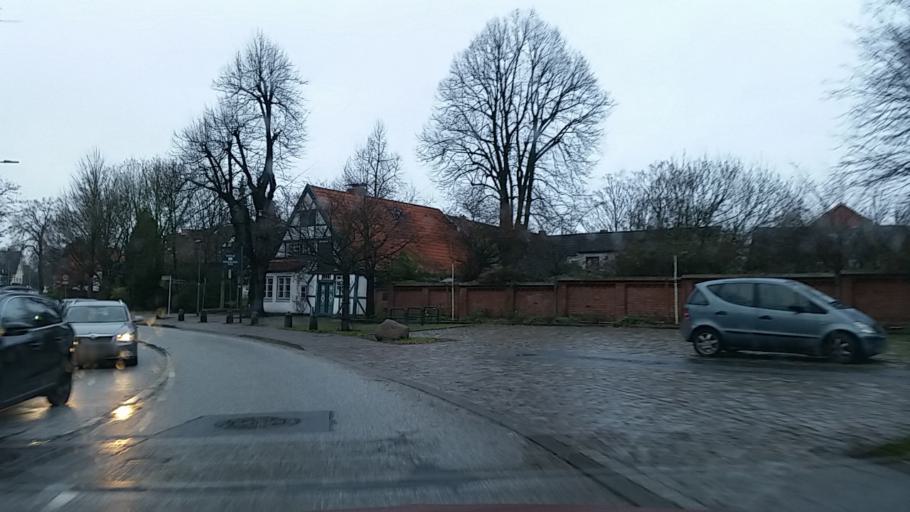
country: DE
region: Schleswig-Holstein
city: Wedel
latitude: 53.5860
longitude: 9.6933
